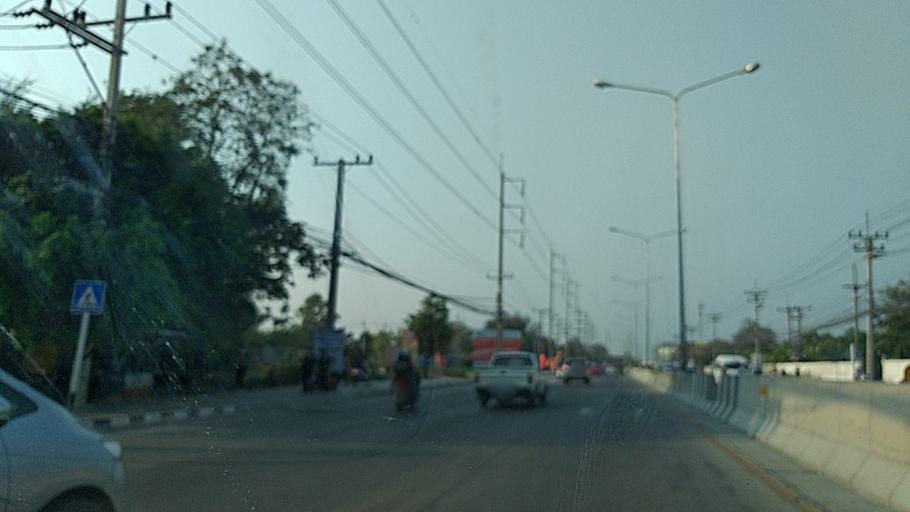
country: TH
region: Phra Nakhon Si Ayutthaya
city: Ban Bang Kadi Pathum Thani
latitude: 13.9895
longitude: 100.5506
